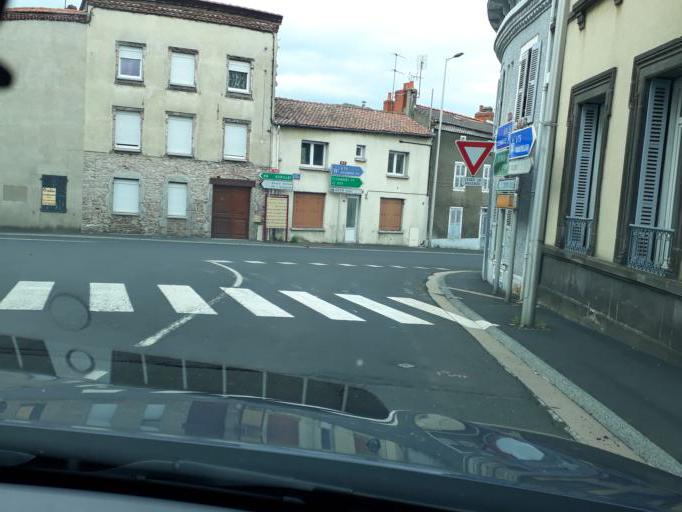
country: FR
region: Auvergne
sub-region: Departement du Cantal
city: Massiac
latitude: 45.2509
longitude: 3.1973
